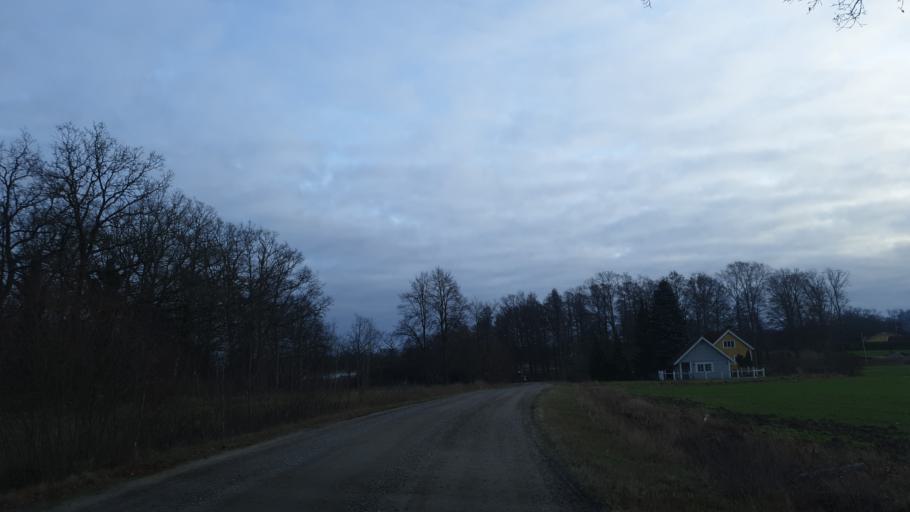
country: SE
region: Kalmar
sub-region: Torsas Kommun
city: Torsas
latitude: 56.3108
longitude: 16.0397
